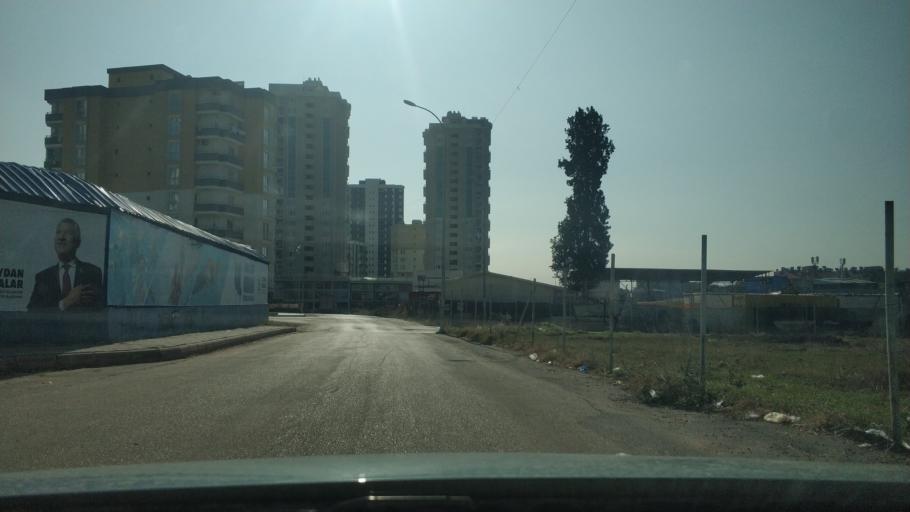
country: TR
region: Adana
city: Seyhan
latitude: 37.0192
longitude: 35.2851
